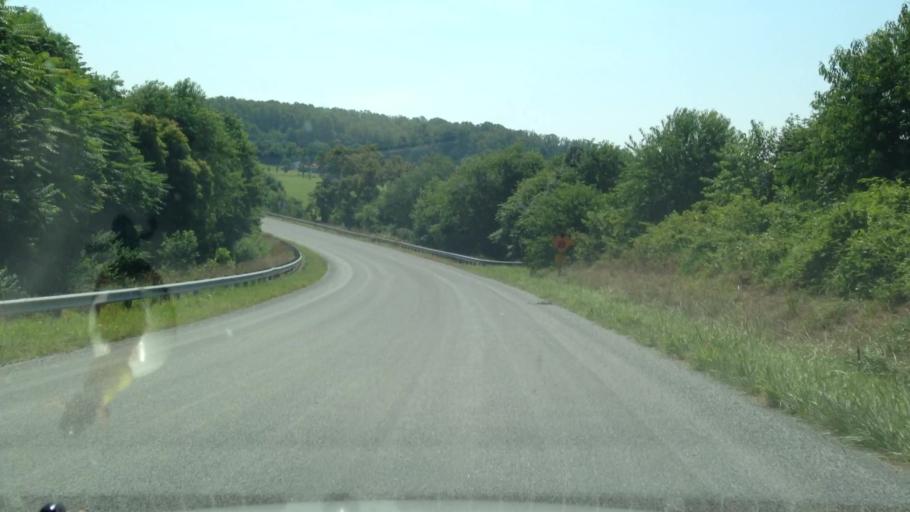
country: US
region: Virginia
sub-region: Patrick County
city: Stuart
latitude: 36.5890
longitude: -80.2849
